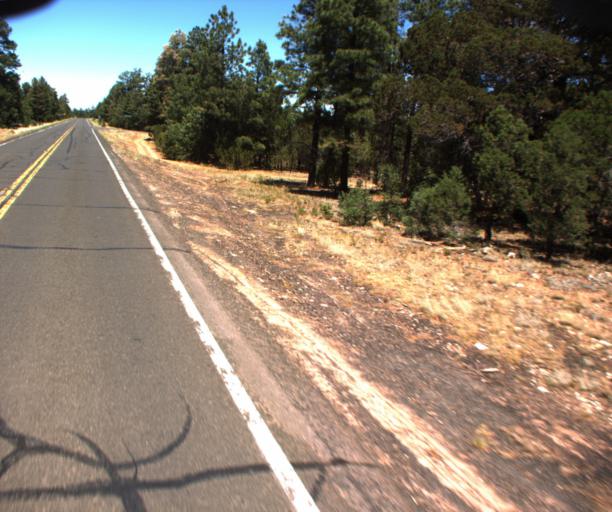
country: US
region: Arizona
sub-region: Gila County
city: Star Valley
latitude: 34.6428
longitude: -111.1102
